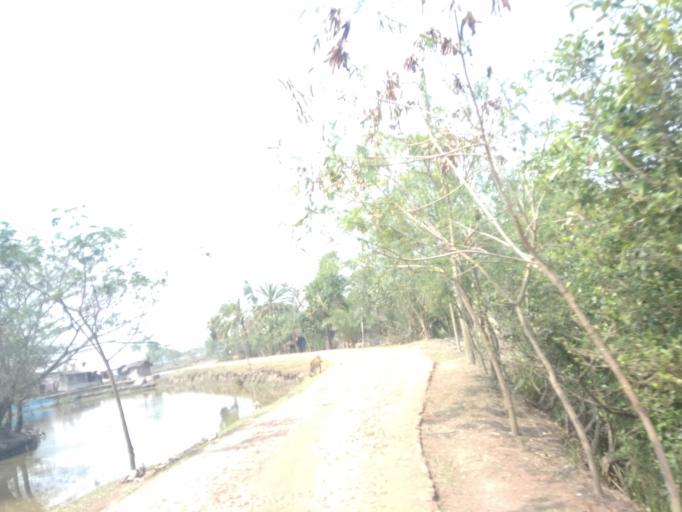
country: IN
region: West Bengal
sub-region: North 24 Parganas
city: Taki
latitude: 22.3000
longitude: 89.2689
